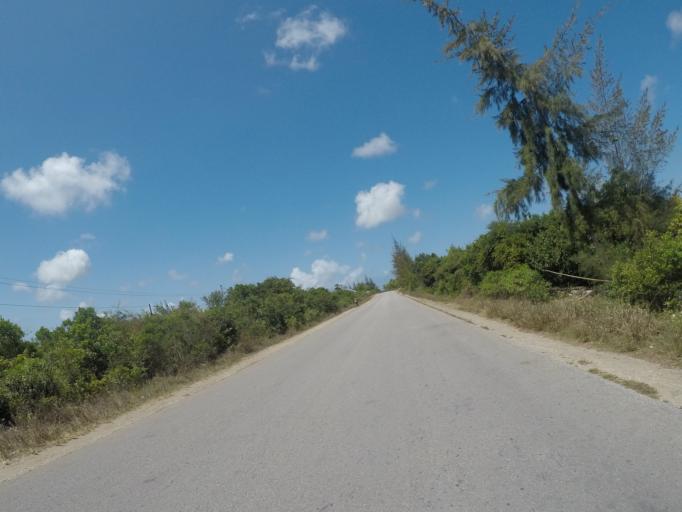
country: TZ
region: Zanzibar Central/South
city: Nganane
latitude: -6.2827
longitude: 39.4686
